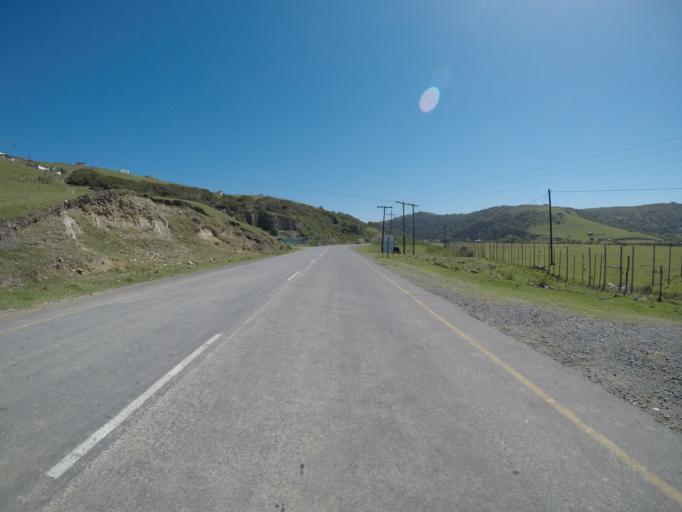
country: ZA
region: Eastern Cape
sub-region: OR Tambo District Municipality
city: Libode
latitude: -31.9829
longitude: 29.1476
